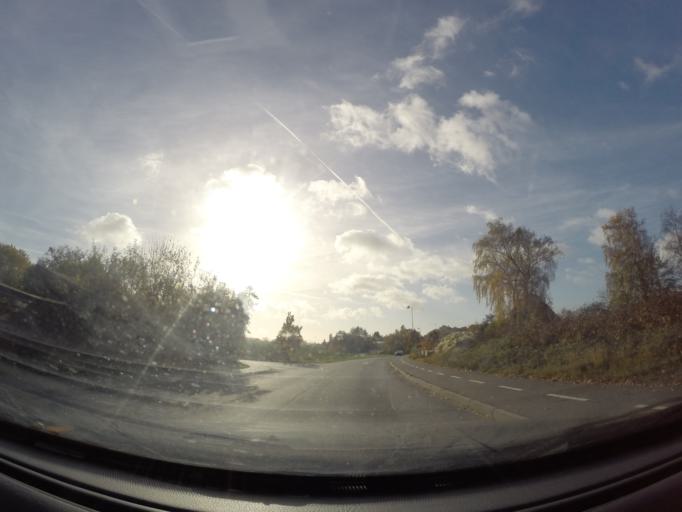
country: DK
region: South Denmark
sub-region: Svendborg Kommune
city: Svendborg
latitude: 55.0687
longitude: 10.5016
